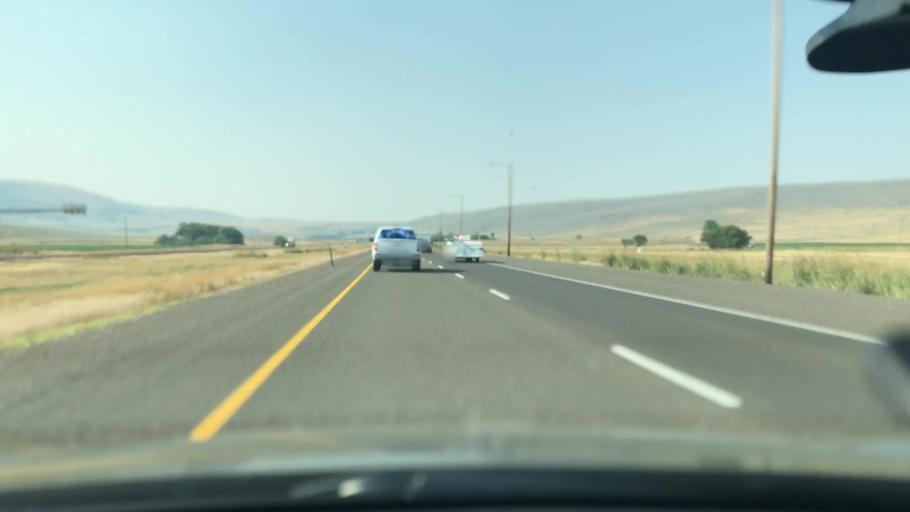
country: US
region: Oregon
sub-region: Union County
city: Union
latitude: 45.1137
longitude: -117.9589
